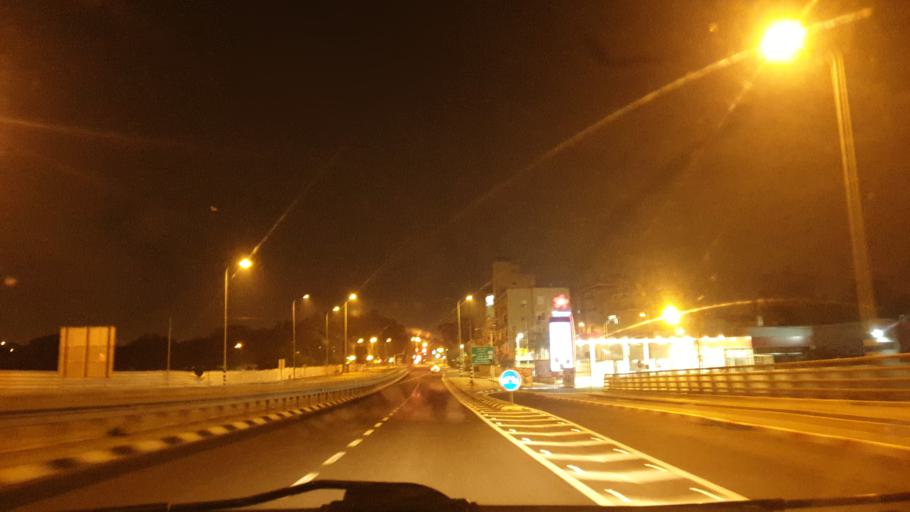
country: IL
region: Central District
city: Ramla
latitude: 31.9408
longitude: 34.8652
